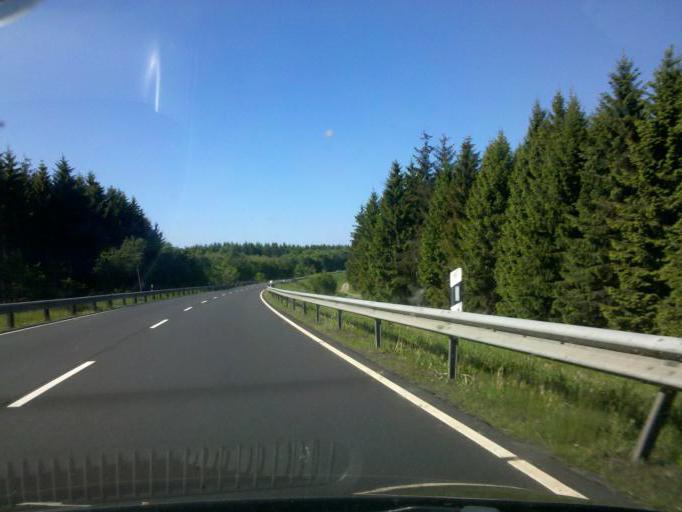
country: DE
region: Rheinland-Pfalz
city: Stein-Neukirch
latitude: 50.6814
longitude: 8.0606
